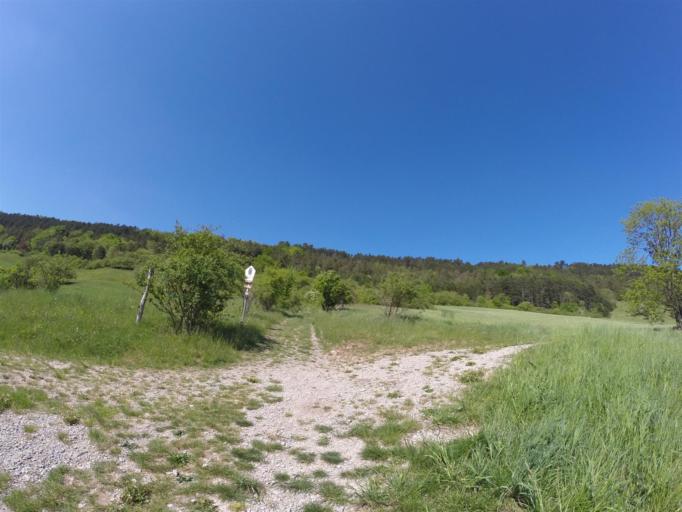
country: DE
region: Thuringia
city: Grosslobichau
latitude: 50.9360
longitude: 11.6617
